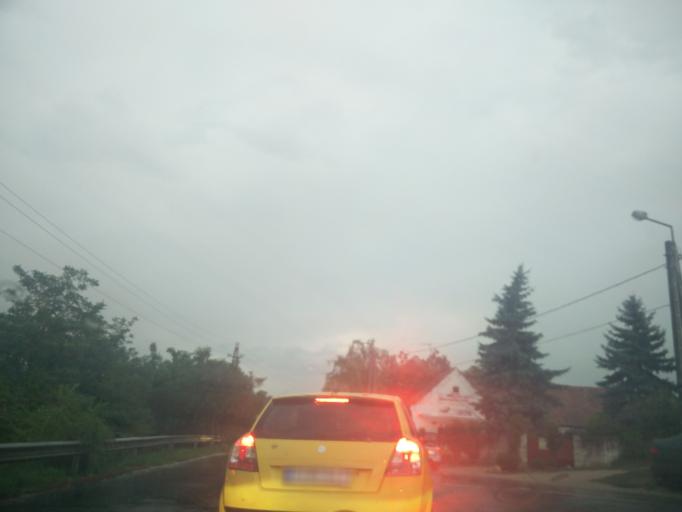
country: HU
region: Pest
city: Biatorbagy
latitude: 47.4587
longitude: 18.8109
